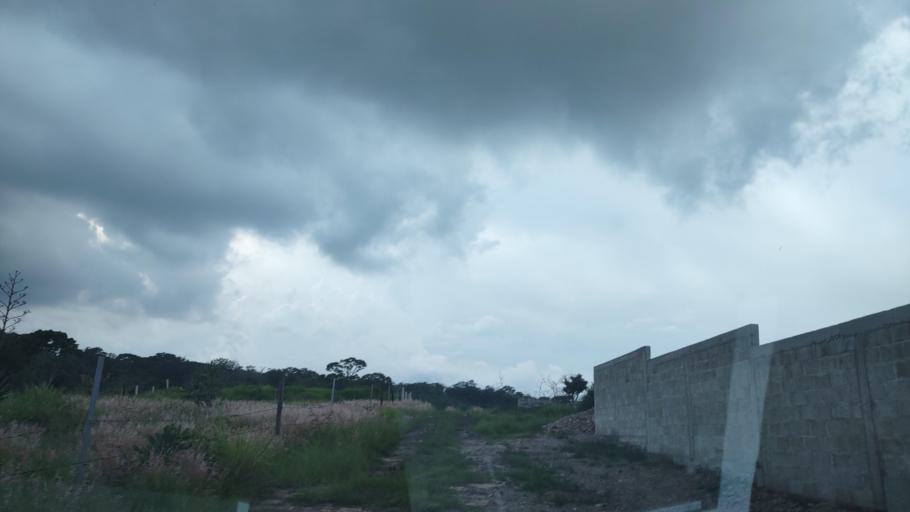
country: MX
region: Veracruz
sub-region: Emiliano Zapata
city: Dos Rios
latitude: 19.4778
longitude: -96.8201
